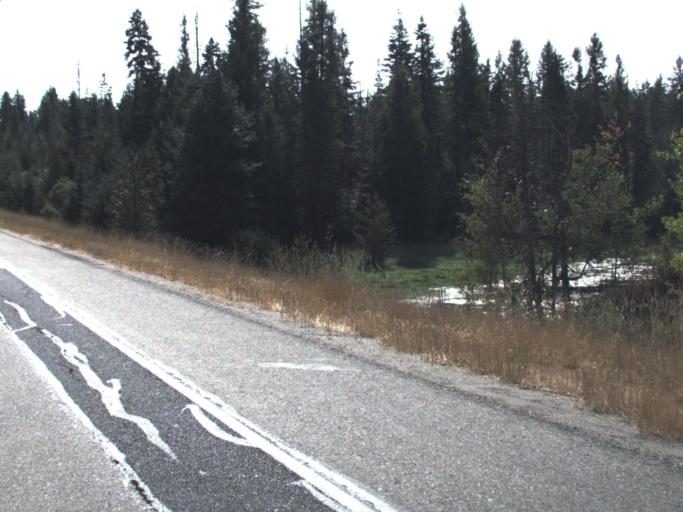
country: US
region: Washington
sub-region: Stevens County
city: Chewelah
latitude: 48.1219
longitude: -117.6496
